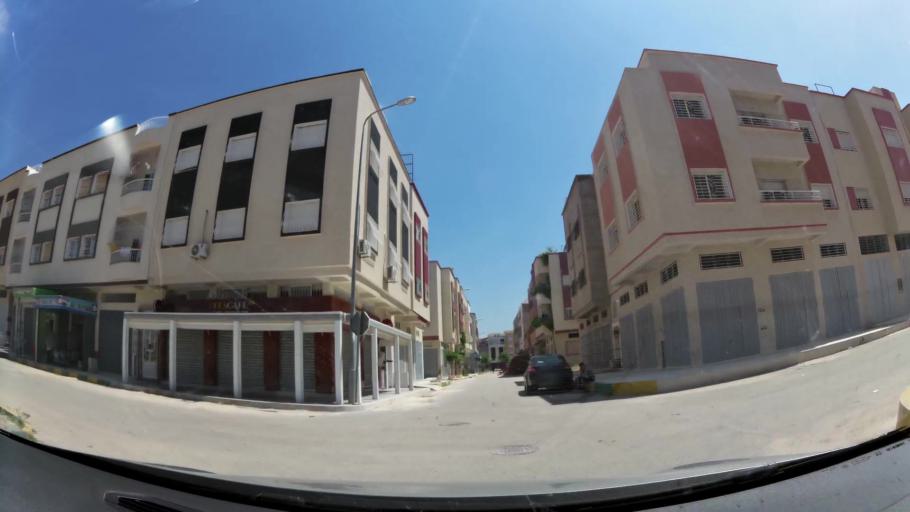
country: MA
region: Fes-Boulemane
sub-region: Fes
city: Fes
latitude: 34.0198
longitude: -5.0511
